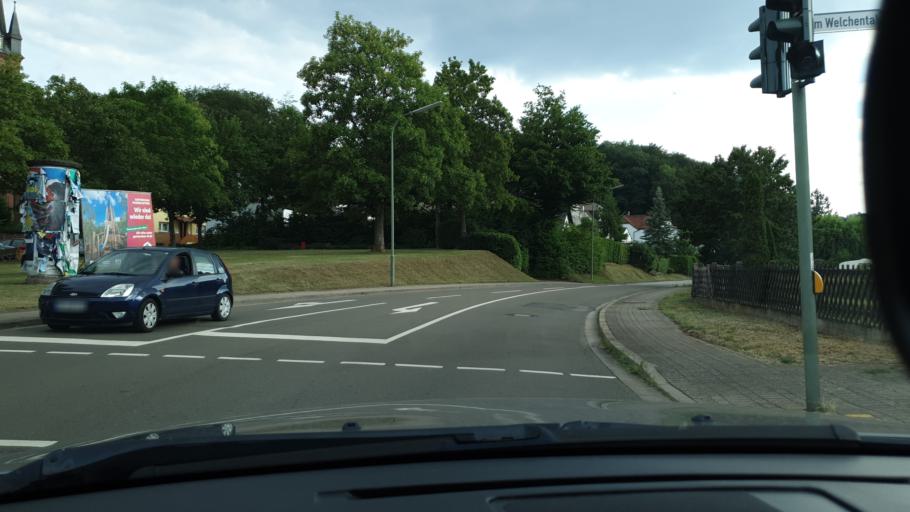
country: DE
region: Rheinland-Pfalz
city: Otterbach
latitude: 49.4802
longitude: 7.7697
